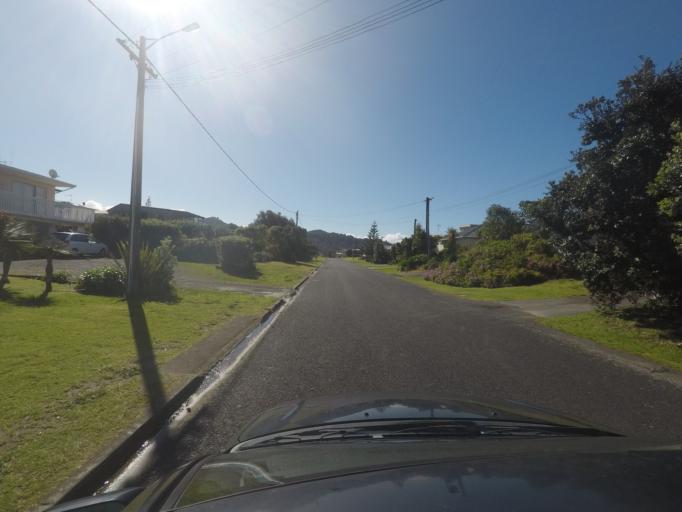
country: NZ
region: Bay of Plenty
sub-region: Western Bay of Plenty District
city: Waihi Beach
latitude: -37.4103
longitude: 175.9457
